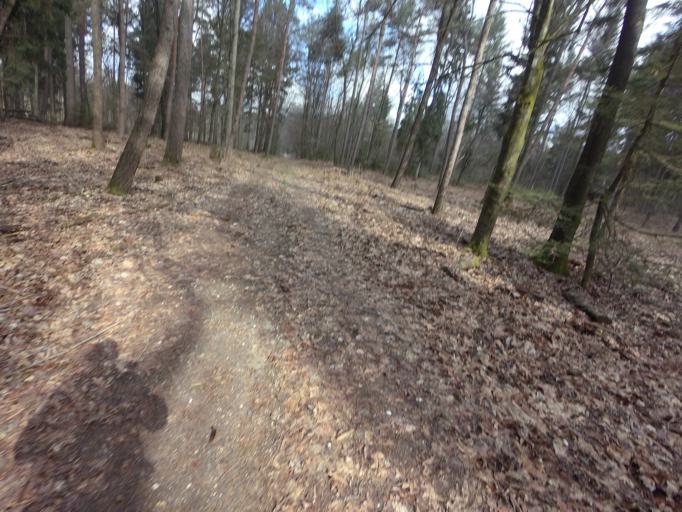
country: NL
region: Limburg
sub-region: Gemeente Roerdalen
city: Herkenbosch
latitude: 51.1746
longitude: 6.0956
